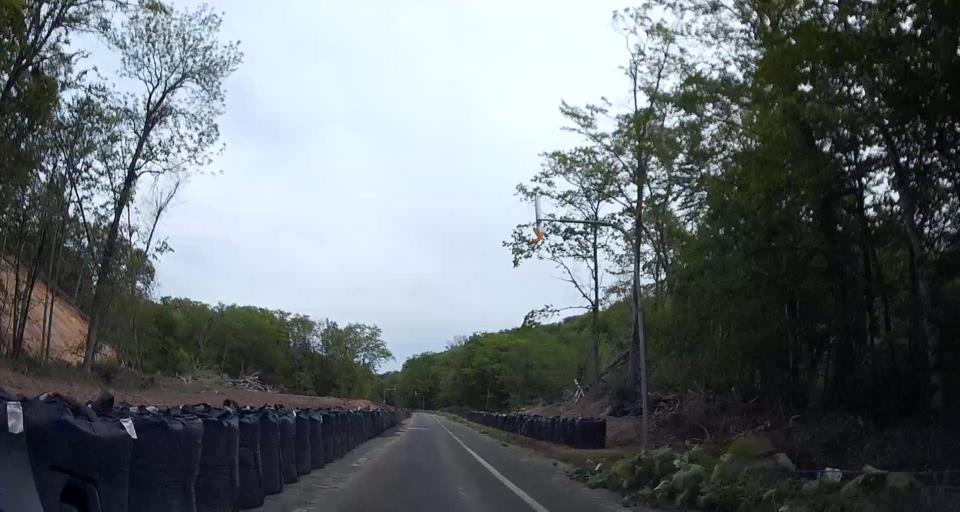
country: JP
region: Hokkaido
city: Chitose
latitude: 42.7923
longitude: 142.0573
